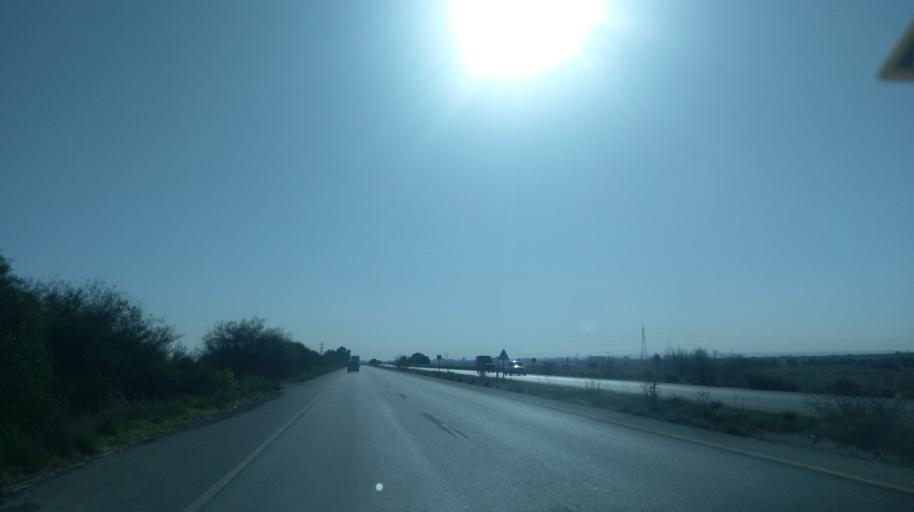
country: CY
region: Ammochostos
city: Lefkonoiko
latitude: 35.2061
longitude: 33.5966
